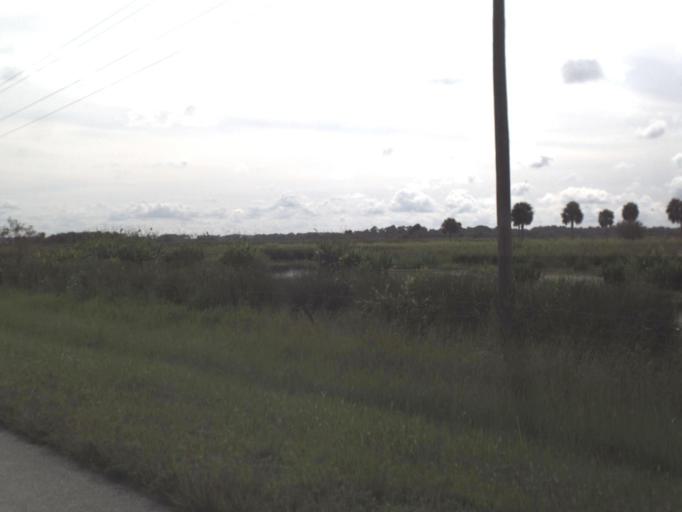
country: US
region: Florida
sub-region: Highlands County
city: Placid Lakes
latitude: 27.2090
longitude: -81.4392
